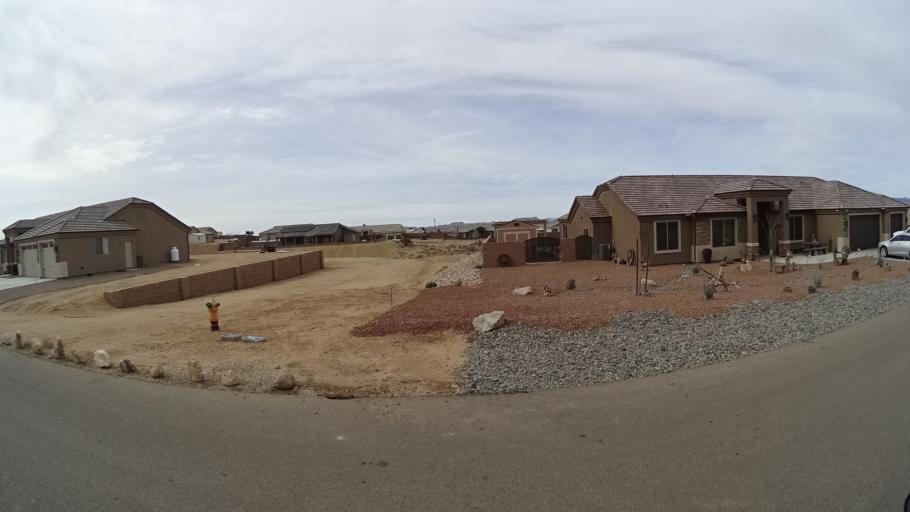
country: US
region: Arizona
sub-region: Mohave County
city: Kingman
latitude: 35.1832
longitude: -113.9766
